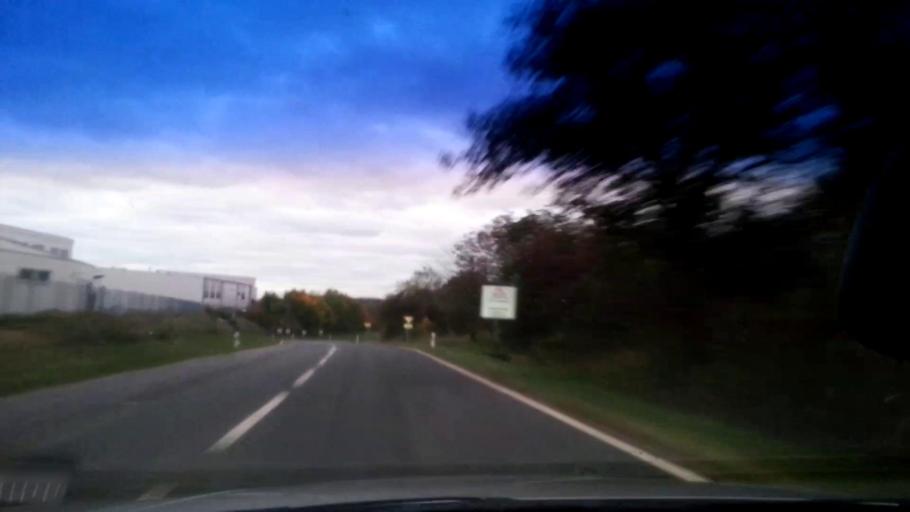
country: DE
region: Bavaria
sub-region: Upper Franconia
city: Schesslitz
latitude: 49.9816
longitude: 11.0471
